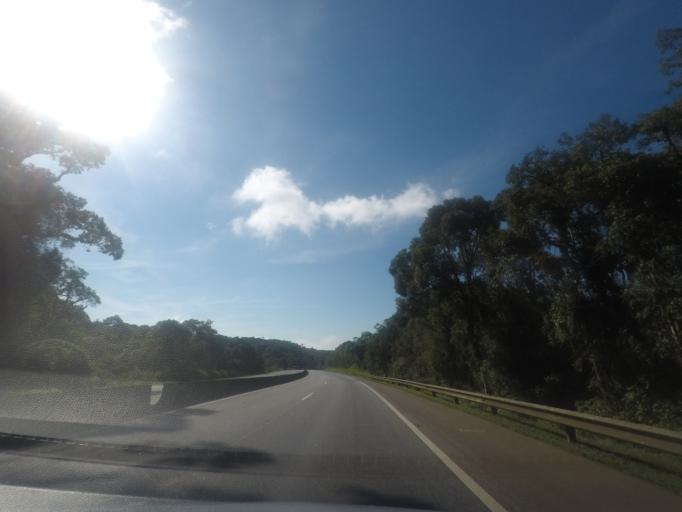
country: BR
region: Parana
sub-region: Piraquara
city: Piraquara
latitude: -25.5918
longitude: -48.9260
